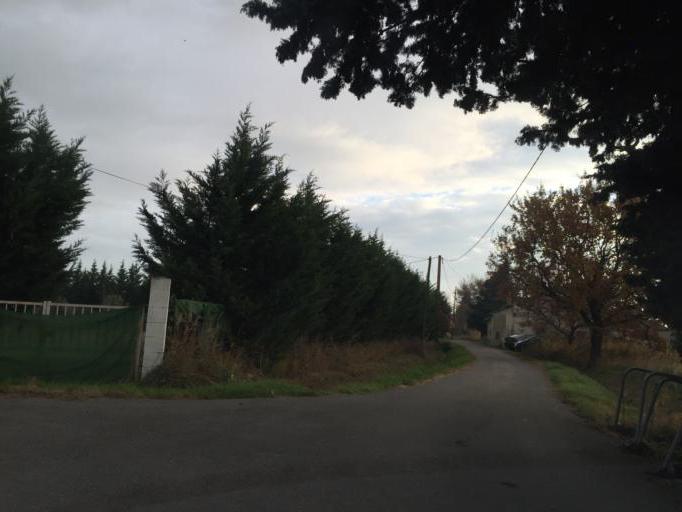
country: FR
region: Provence-Alpes-Cote d'Azur
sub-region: Departement du Vaucluse
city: Jonquieres
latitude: 44.1078
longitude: 4.8834
